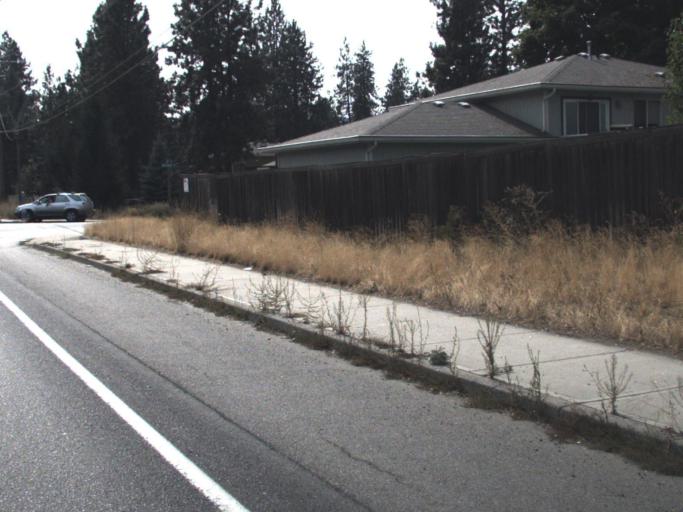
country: US
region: Washington
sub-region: Spokane County
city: Fairwood
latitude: 47.7634
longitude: -117.4066
